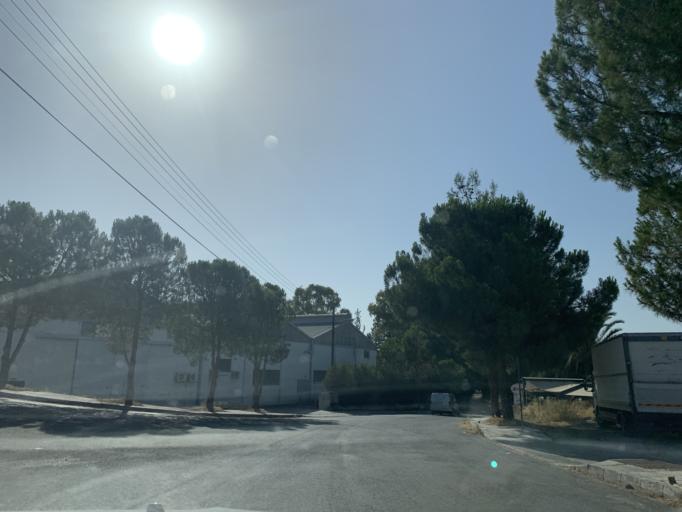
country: CY
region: Lefkosia
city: Nicosia
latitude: 35.1252
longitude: 33.3603
